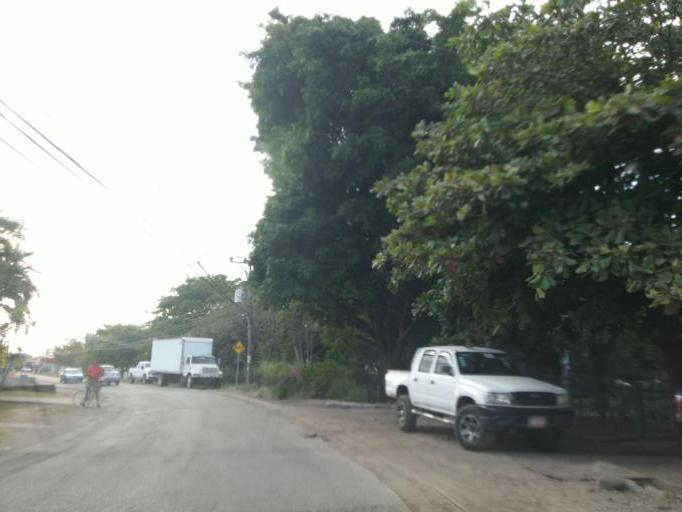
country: CR
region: Heredia
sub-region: Canton de Belen
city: San Antonio
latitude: 9.9756
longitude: -84.2197
